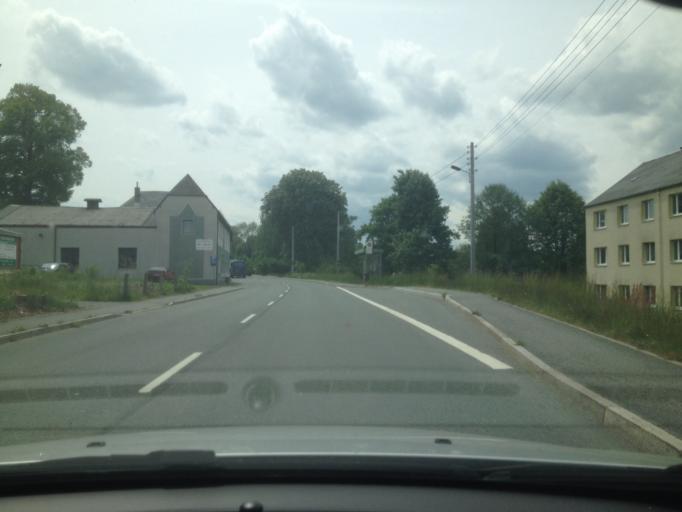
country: DE
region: Saxony
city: Stollberg
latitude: 50.6907
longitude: 12.7664
